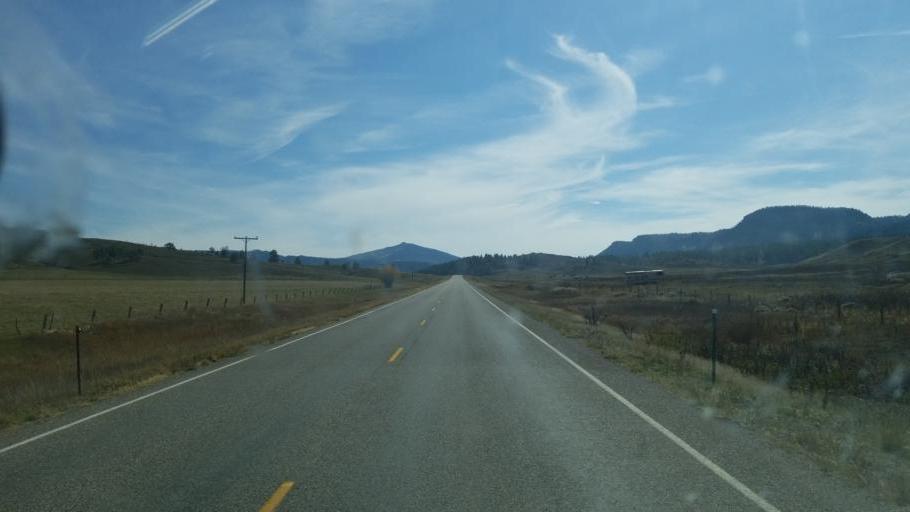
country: US
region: New Mexico
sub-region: Rio Arriba County
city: Dulce
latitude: 37.0286
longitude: -106.8260
